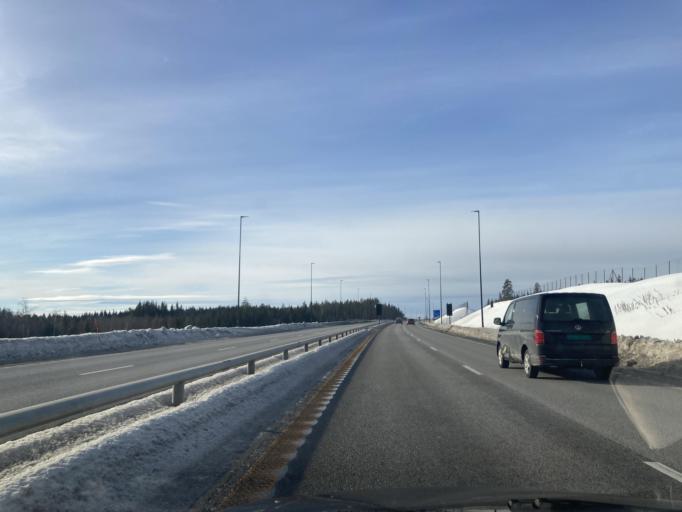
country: NO
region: Hedmark
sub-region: Loten
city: Loten
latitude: 60.8541
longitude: 11.3930
